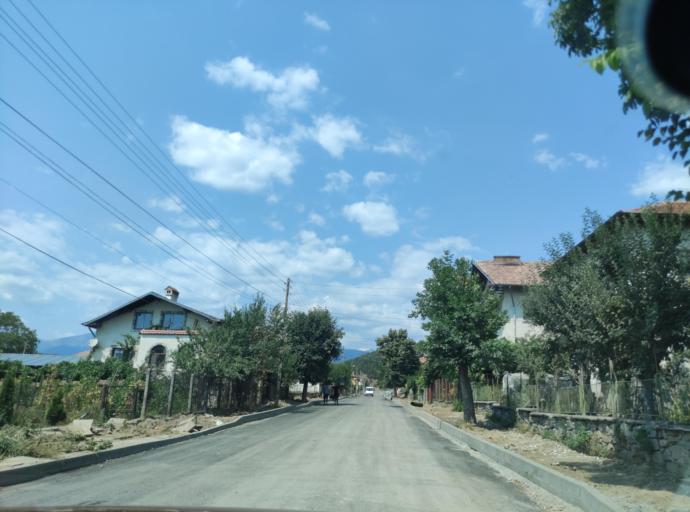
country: BG
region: Blagoevgrad
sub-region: Obshtina Belitsa
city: Belitsa
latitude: 41.9446
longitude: 23.5650
